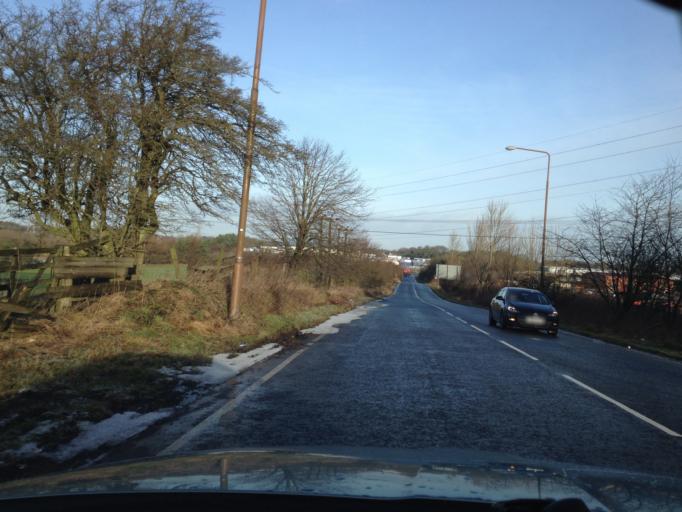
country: GB
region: Scotland
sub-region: West Lothian
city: Whitburn
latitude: 55.8811
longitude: -3.6614
